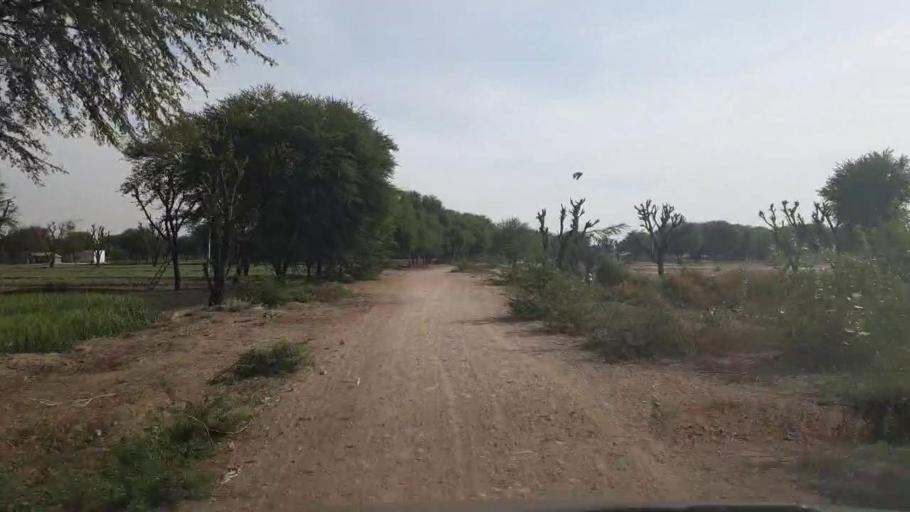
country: PK
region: Sindh
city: Umarkot
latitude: 25.2946
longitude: 69.7080
